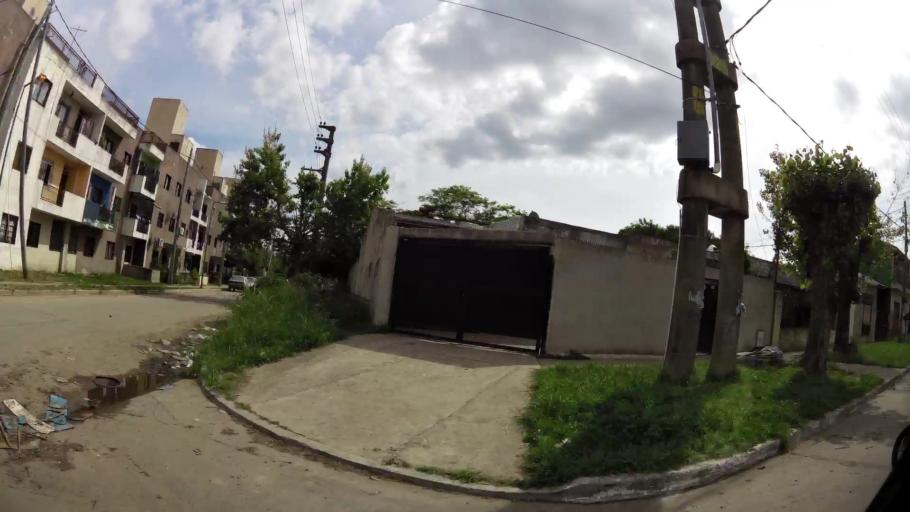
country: AR
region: Buenos Aires
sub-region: Partido de Quilmes
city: Quilmes
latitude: -34.7500
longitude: -58.2500
